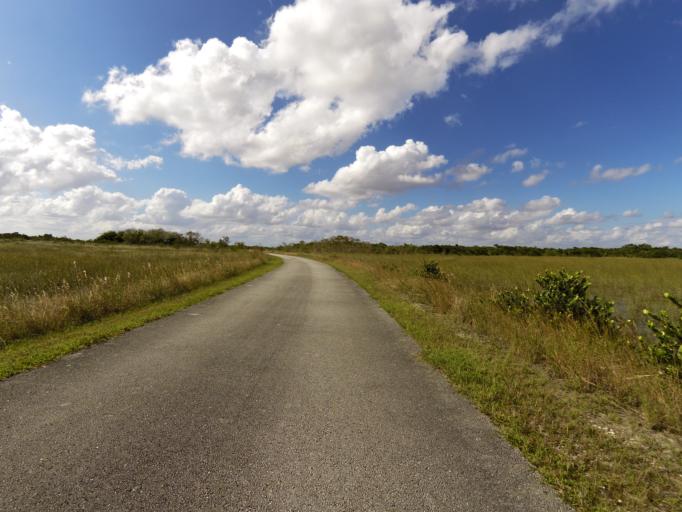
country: US
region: Florida
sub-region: Miami-Dade County
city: The Hammocks
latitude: 25.7171
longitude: -80.7599
